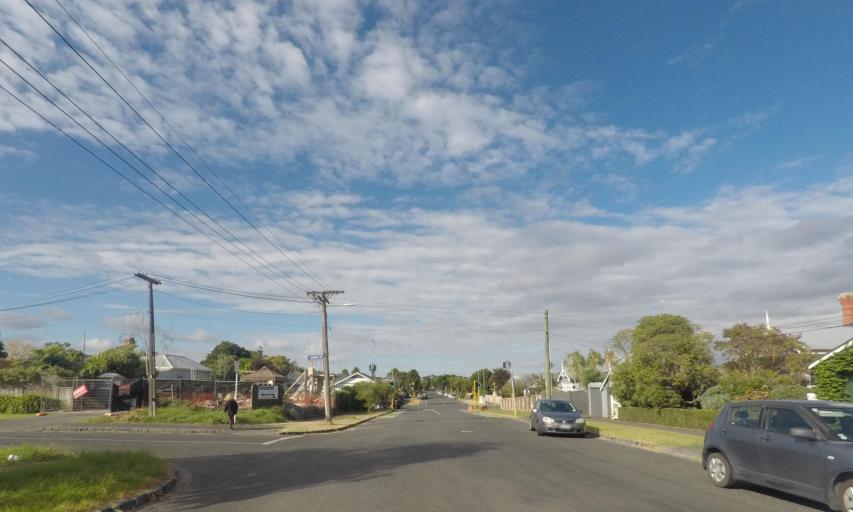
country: NZ
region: Auckland
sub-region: Auckland
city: Auckland
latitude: -36.8855
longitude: 174.7437
